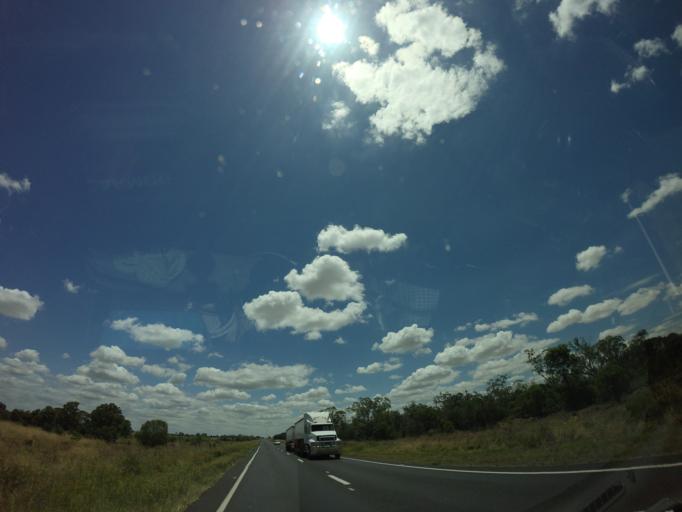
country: AU
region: New South Wales
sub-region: Moree Plains
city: Boggabilla
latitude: -28.7883
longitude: 150.2539
